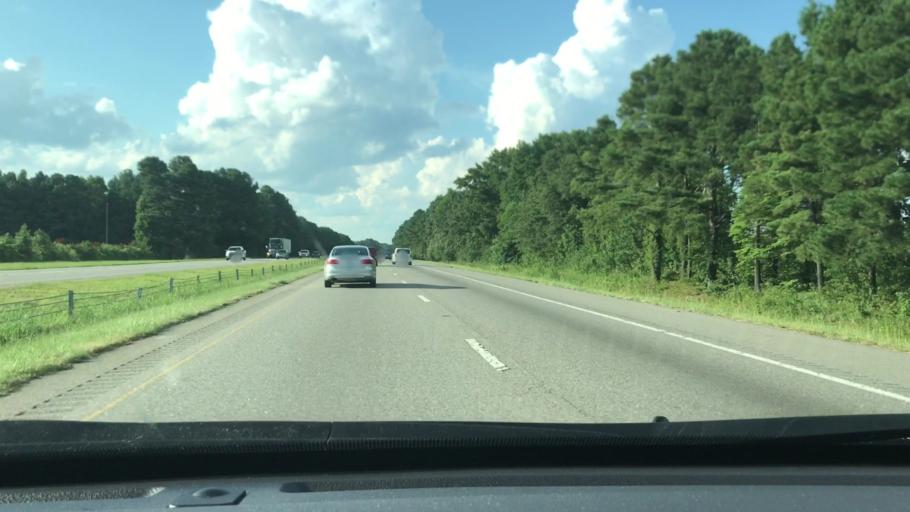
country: US
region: North Carolina
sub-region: Robeson County
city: Saint Pauls
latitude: 34.7543
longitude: -78.9970
